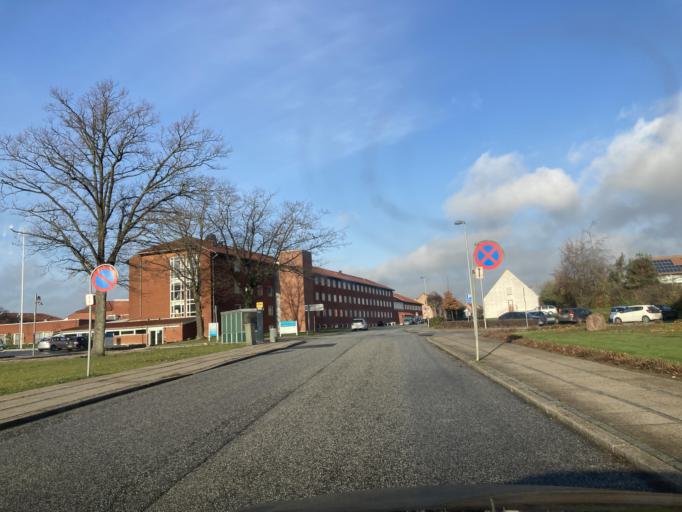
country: DK
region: Zealand
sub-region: Guldborgsund Kommune
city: Nykobing Falster
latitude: 54.7779
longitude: 11.8618
